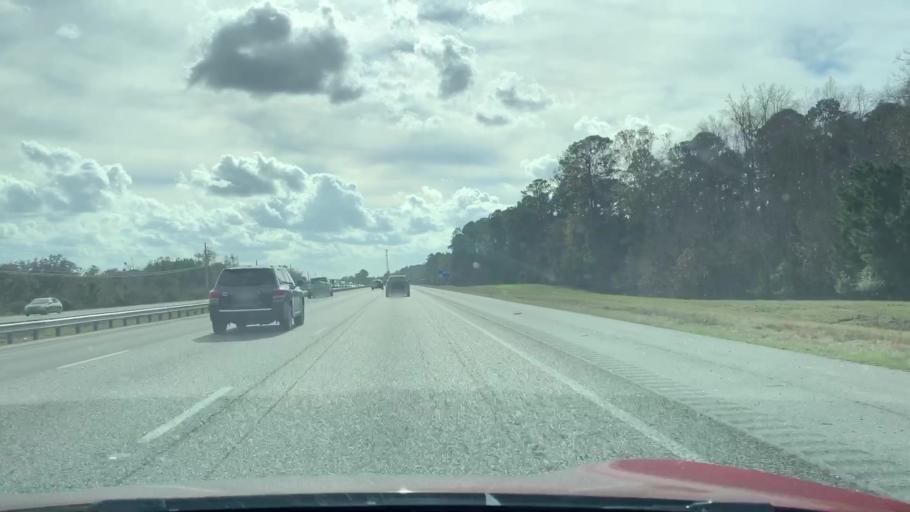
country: US
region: Georgia
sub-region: Liberty County
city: Midway
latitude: 31.8014
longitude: -81.3705
